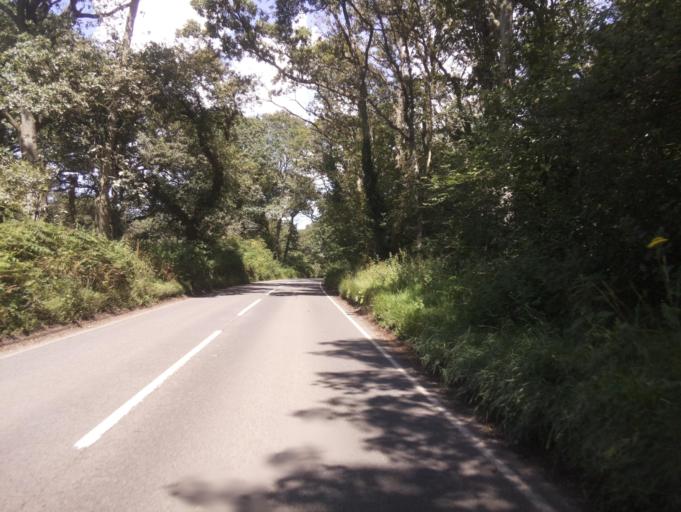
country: GB
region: England
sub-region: West Berkshire
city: Winterbourne
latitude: 51.4456
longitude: -1.3340
